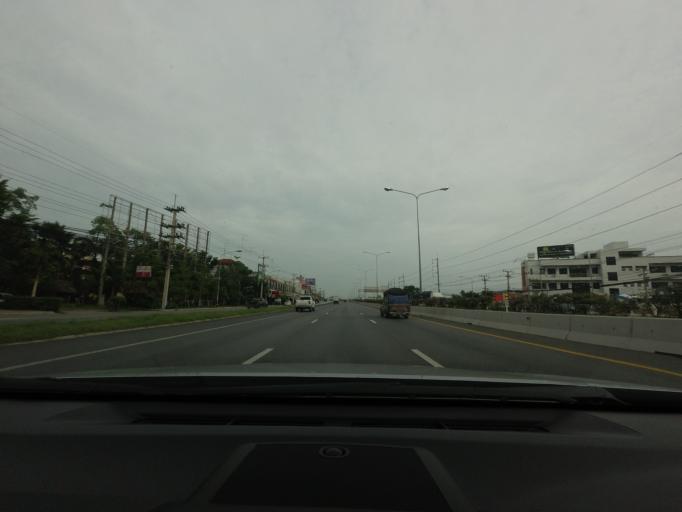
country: TH
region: Phetchaburi
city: Phetchaburi
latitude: 13.1058
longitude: 99.9344
